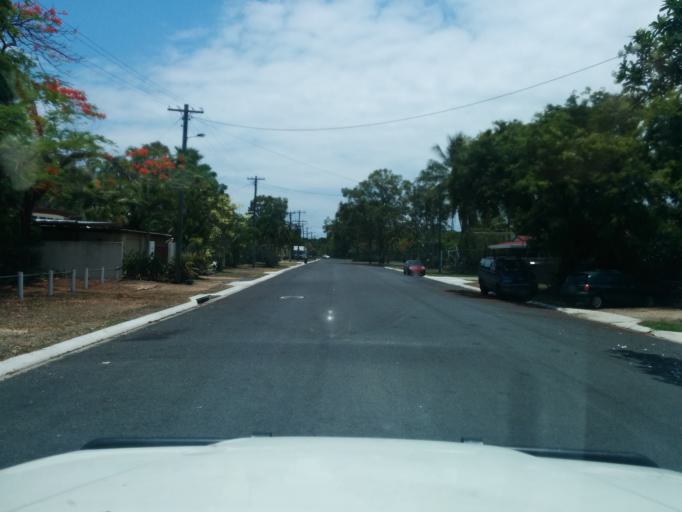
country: AU
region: Queensland
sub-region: Cairns
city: Yorkeys Knob
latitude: -16.8306
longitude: 145.7352
